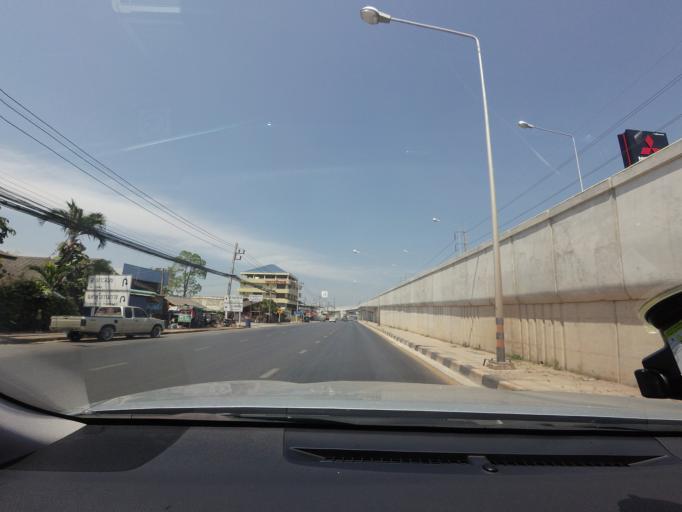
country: TH
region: Surat Thani
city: Surat Thani
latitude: 9.1507
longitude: 99.3721
